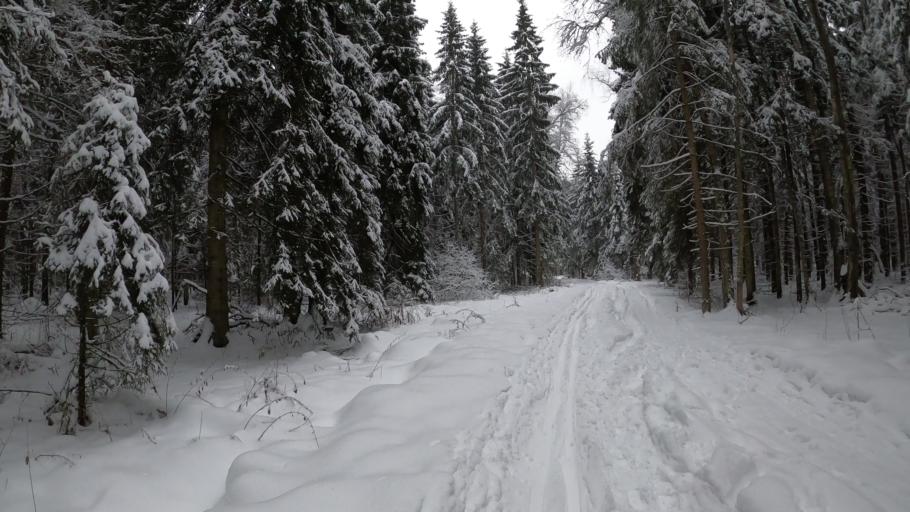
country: RU
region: Moskovskaya
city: Firsanovka
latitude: 55.9569
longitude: 37.2217
